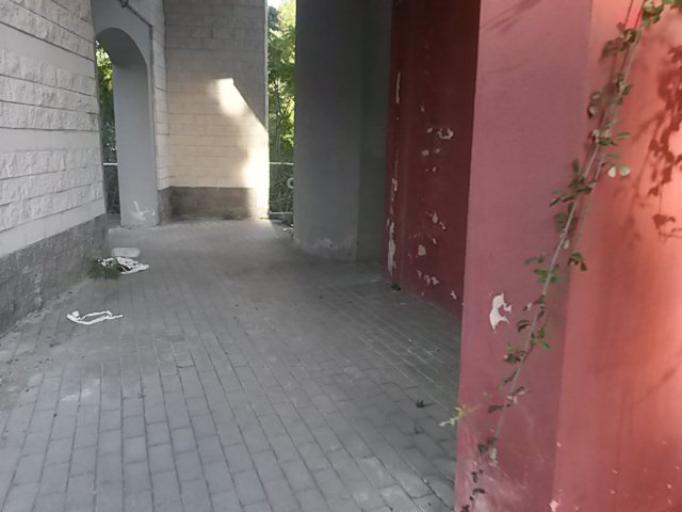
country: IT
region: Calabria
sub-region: Provincia di Catanzaro
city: Catanzaro
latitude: 38.8975
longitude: 16.6004
